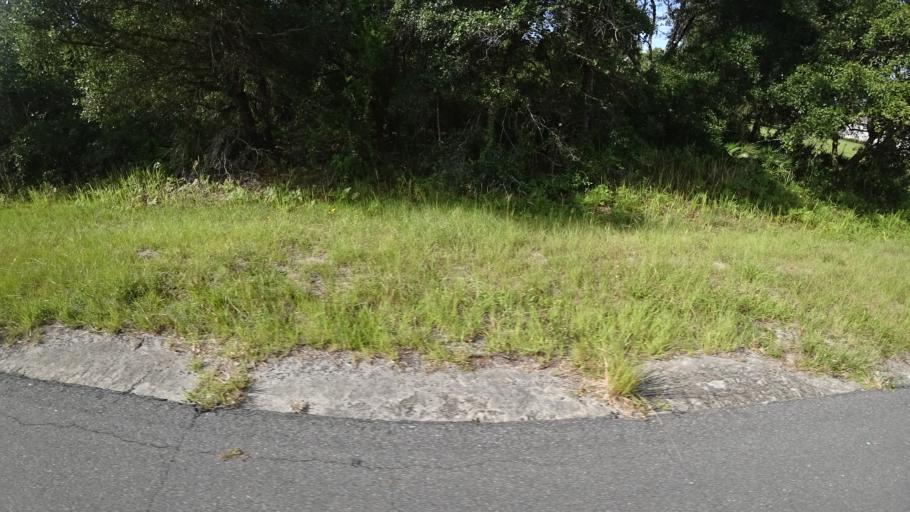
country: US
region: Florida
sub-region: Sarasota County
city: Lake Sarasota
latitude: 27.3518
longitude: -82.2479
